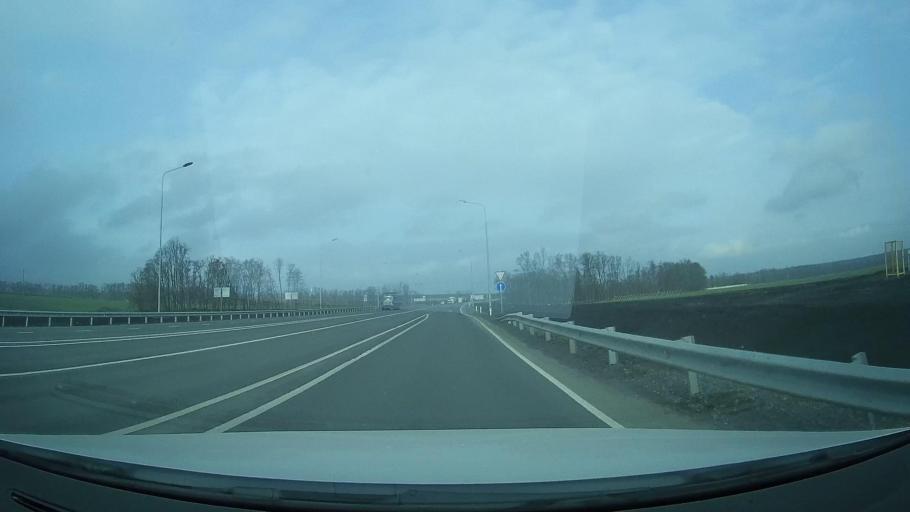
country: RU
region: Rostov
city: Grushevskaya
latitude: 47.3811
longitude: 39.8455
